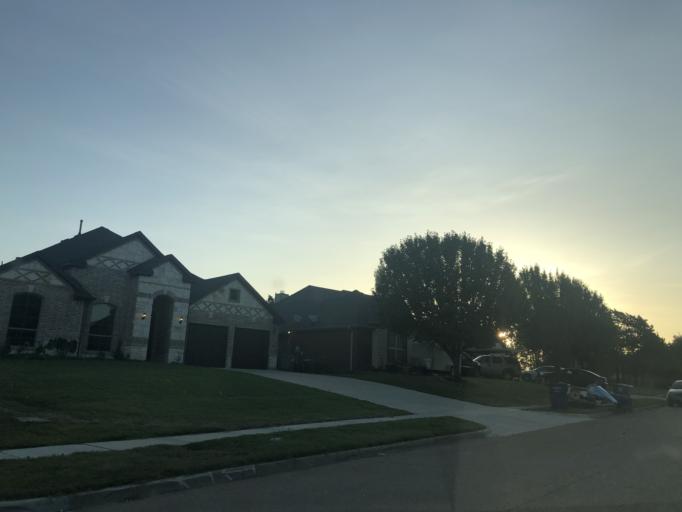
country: US
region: Texas
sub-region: Dallas County
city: Duncanville
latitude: 32.6476
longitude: -96.9564
